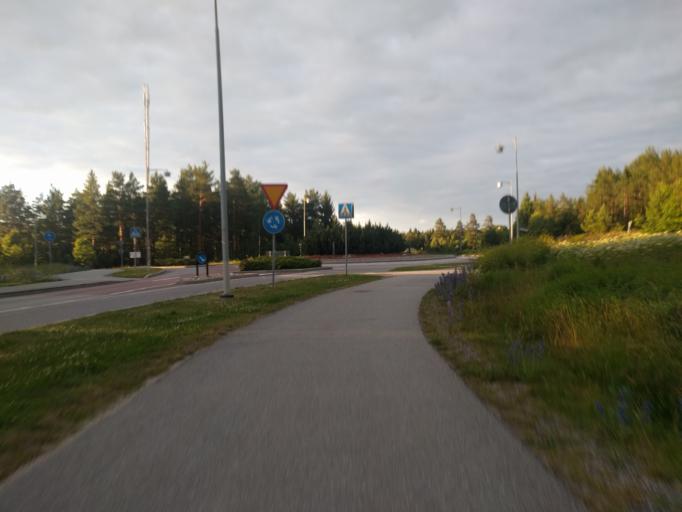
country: SE
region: Stockholm
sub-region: Vallentuna Kommun
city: Vallentuna
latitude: 59.5142
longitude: 18.0783
